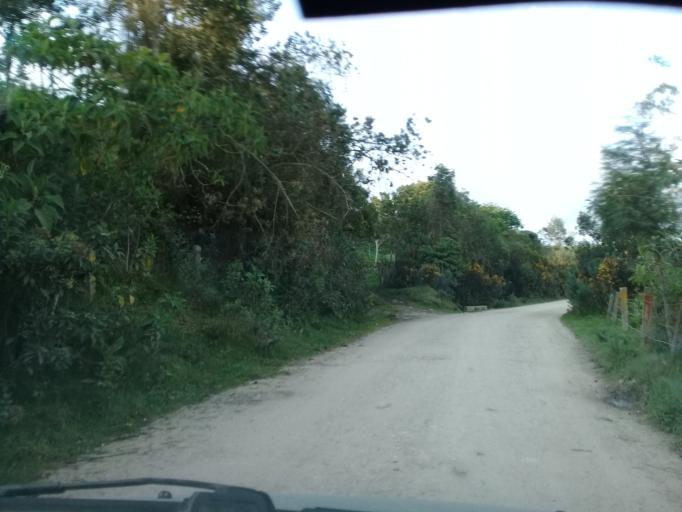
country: CO
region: Cundinamarca
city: Sibate
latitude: 4.4363
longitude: -74.2815
